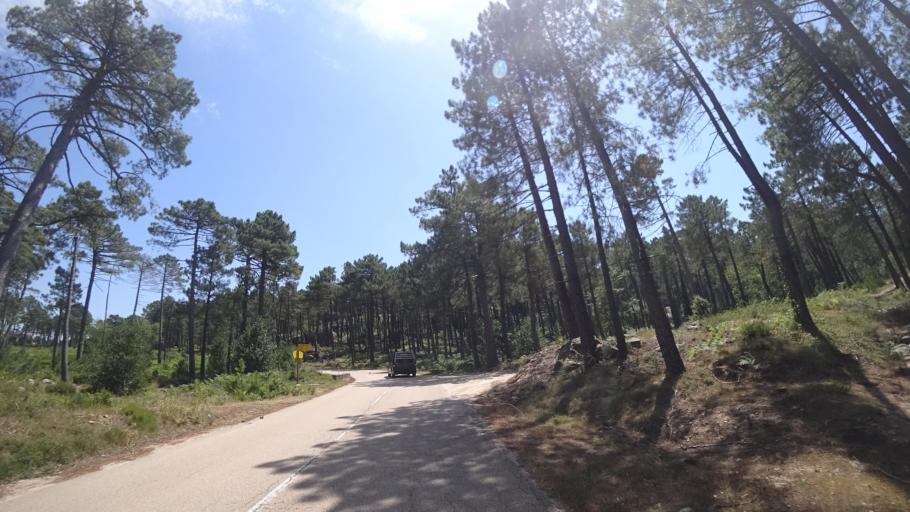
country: FR
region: Corsica
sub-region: Departement de la Corse-du-Sud
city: Zonza
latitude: 41.6859
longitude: 9.1958
